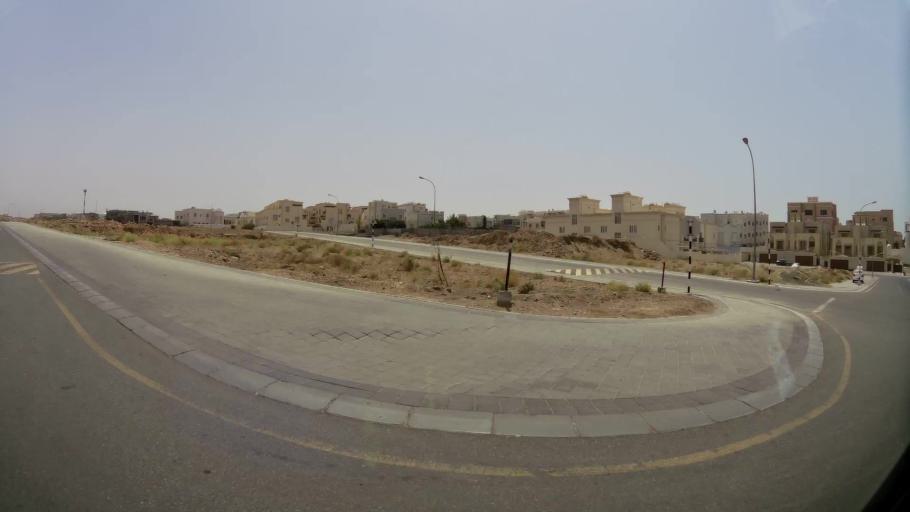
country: OM
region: Muhafazat Masqat
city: Bawshar
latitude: 23.5648
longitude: 58.3999
